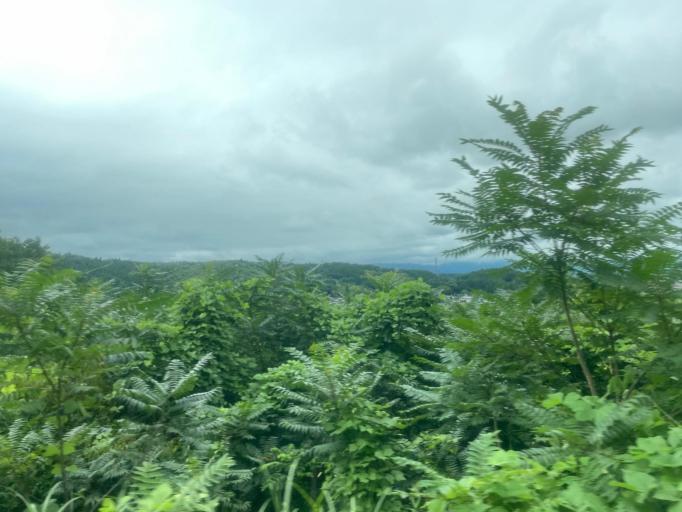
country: JP
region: Fukushima
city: Fukushima-shi
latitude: 37.7003
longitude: 140.4513
